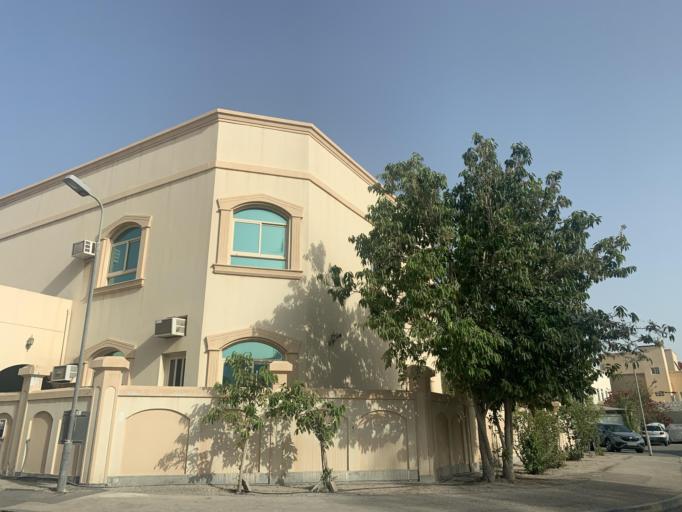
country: BH
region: Manama
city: Jidd Hafs
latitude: 26.2267
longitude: 50.5471
